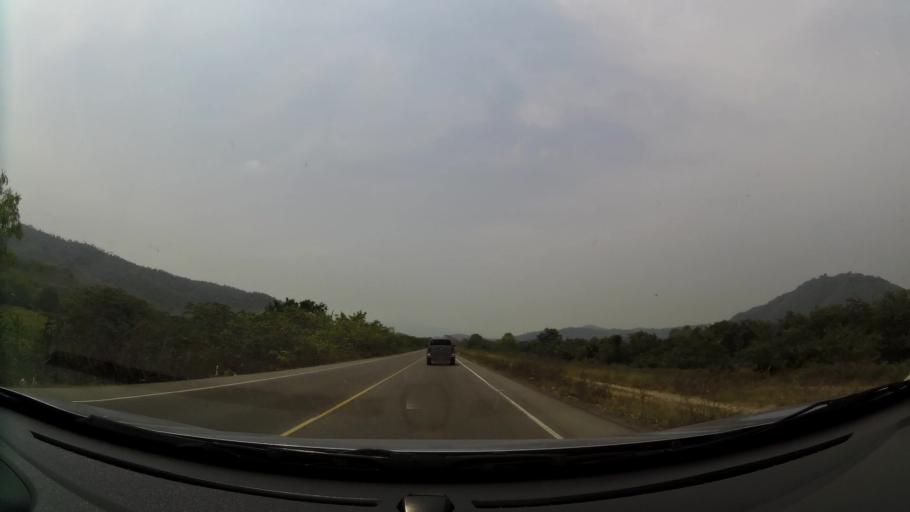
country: HN
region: Cortes
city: Potrerillos
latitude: 15.2522
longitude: -87.9556
